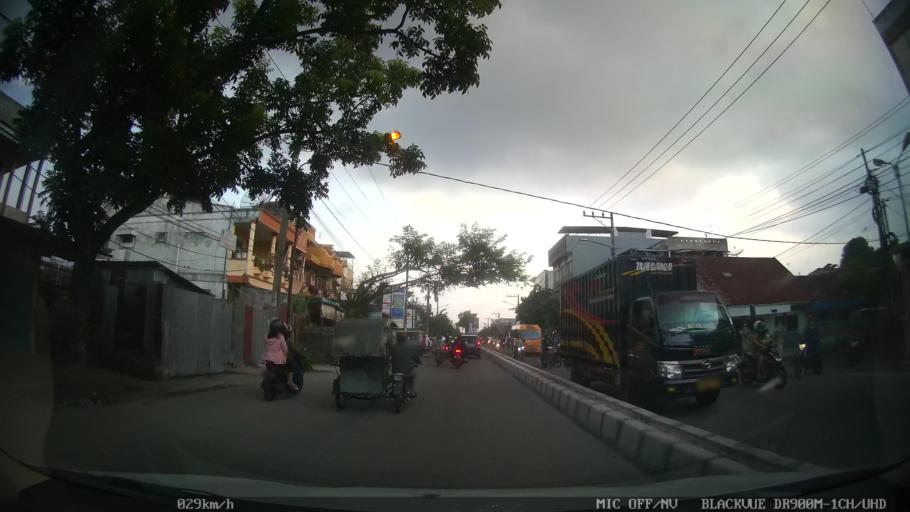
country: ID
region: North Sumatra
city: Medan
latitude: 3.5842
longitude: 98.7112
